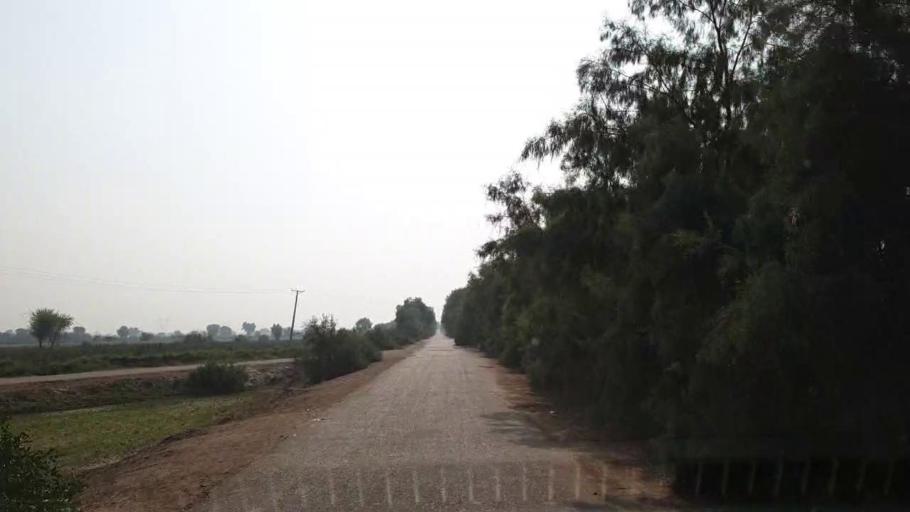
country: PK
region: Sindh
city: Bhan
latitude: 26.4778
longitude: 67.7718
